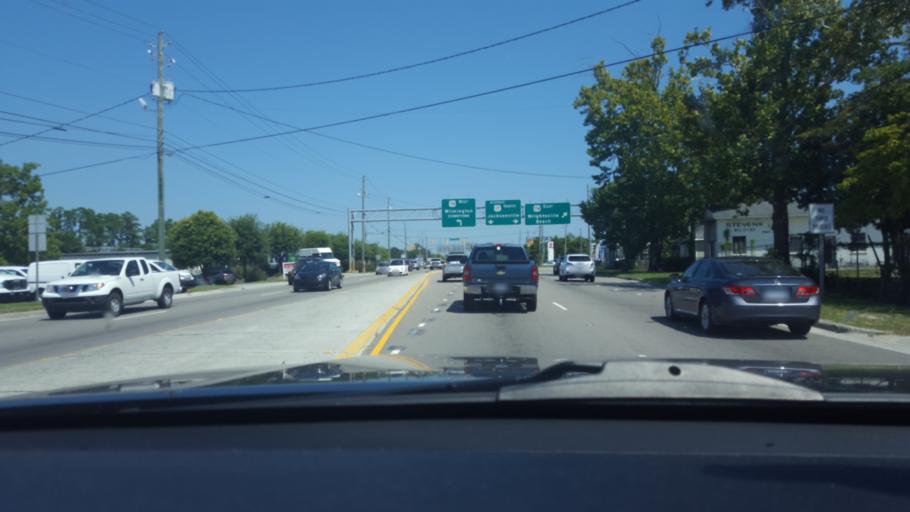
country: US
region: North Carolina
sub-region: New Hanover County
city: Kings Grant
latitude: 34.2473
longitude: -77.8656
